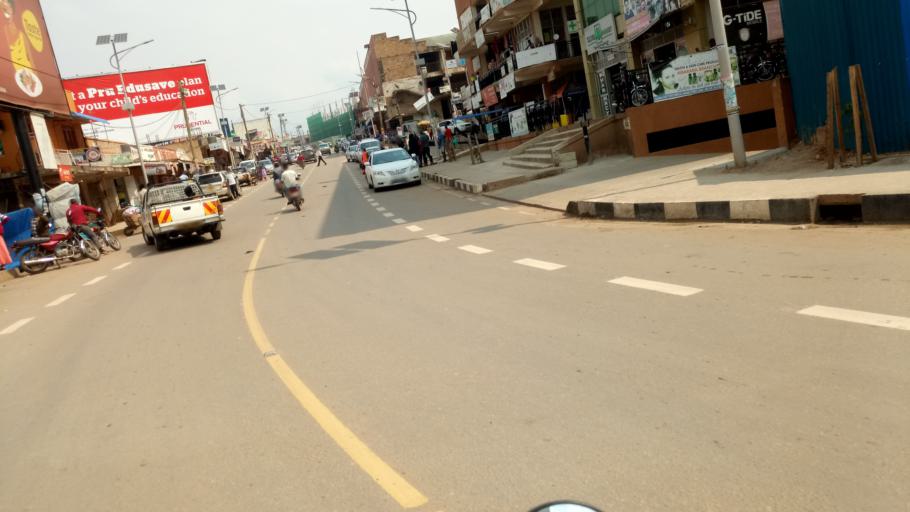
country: UG
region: Western Region
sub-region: Mbarara District
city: Mbarara
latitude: -0.6053
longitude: 30.6642
